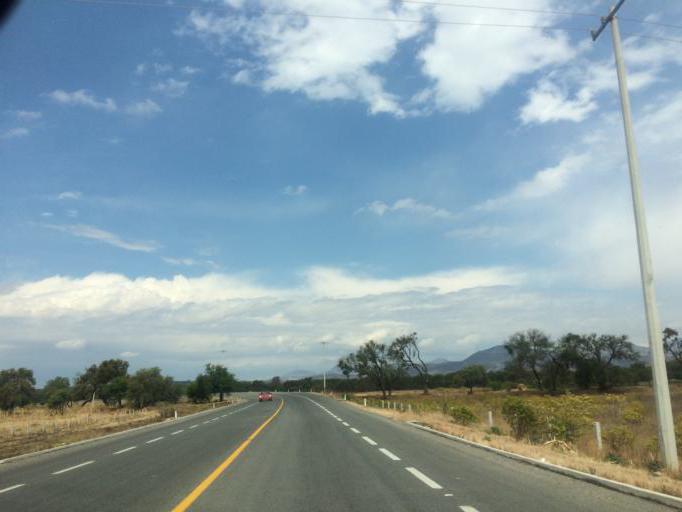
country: MX
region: Guanajuato
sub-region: Silao de la Victoria
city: Loma de Yerbabuena
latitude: 21.0303
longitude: -101.4596
